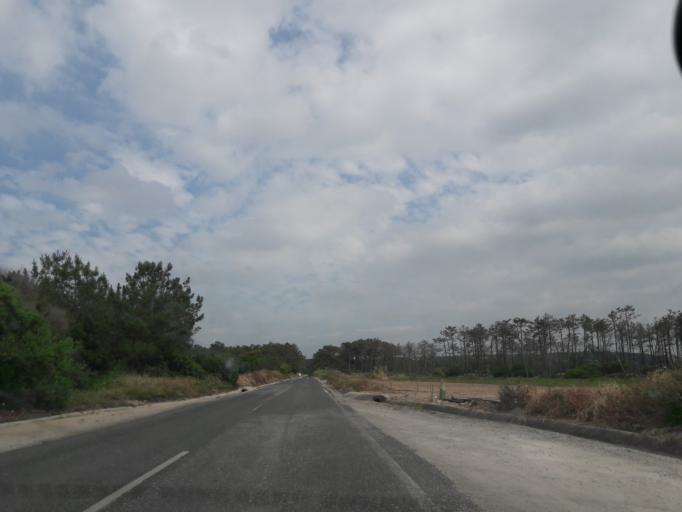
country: PT
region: Leiria
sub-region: Peniche
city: Atouguia da Baleia
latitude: 39.3596
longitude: -9.3045
